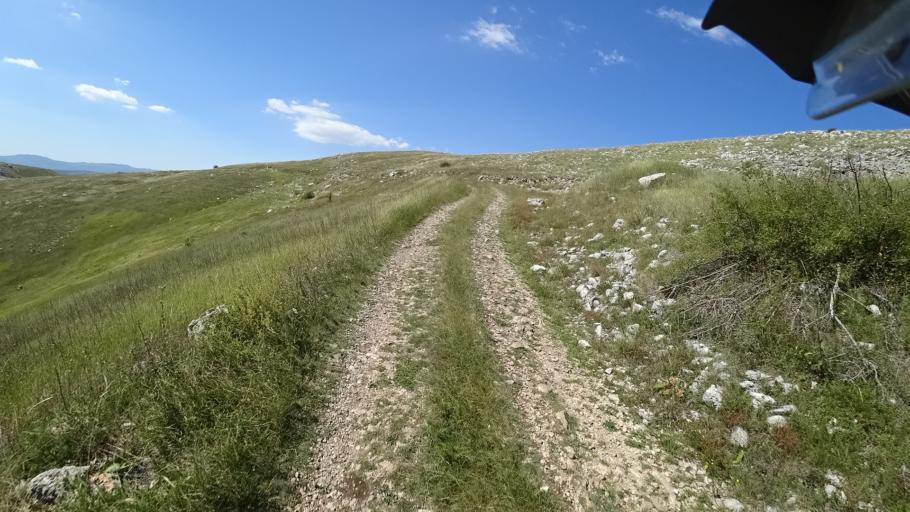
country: HR
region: Splitsko-Dalmatinska
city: Hrvace
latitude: 43.8861
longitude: 16.6429
